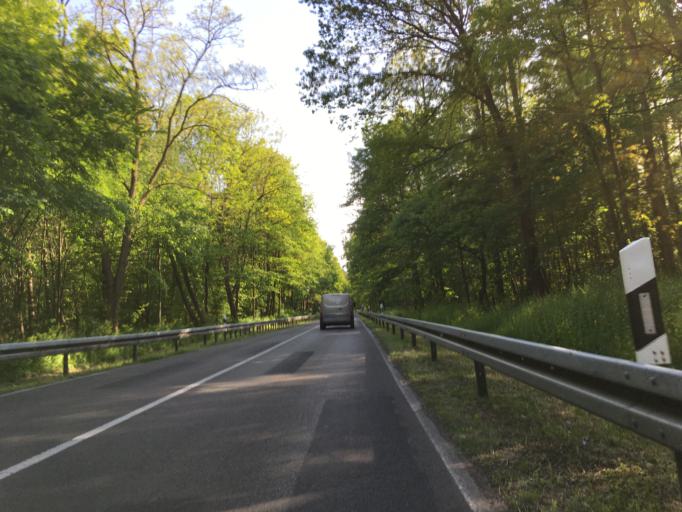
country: DE
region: Brandenburg
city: Protzel
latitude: 52.6107
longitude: 13.9555
